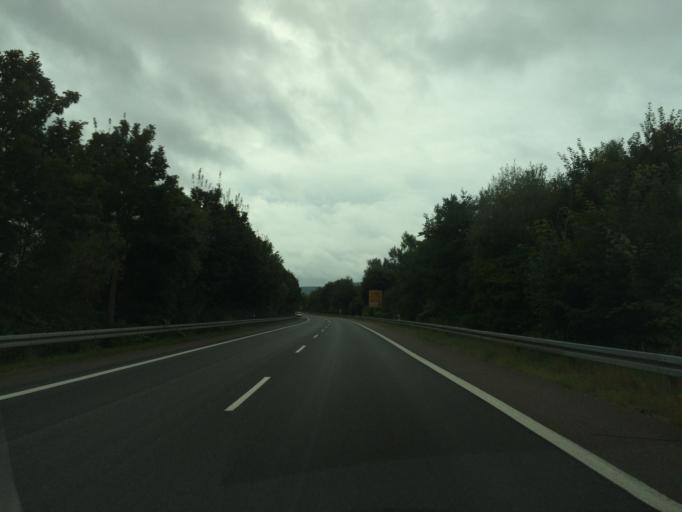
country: DE
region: Saarland
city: Merzig
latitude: 49.4339
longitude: 6.6305
